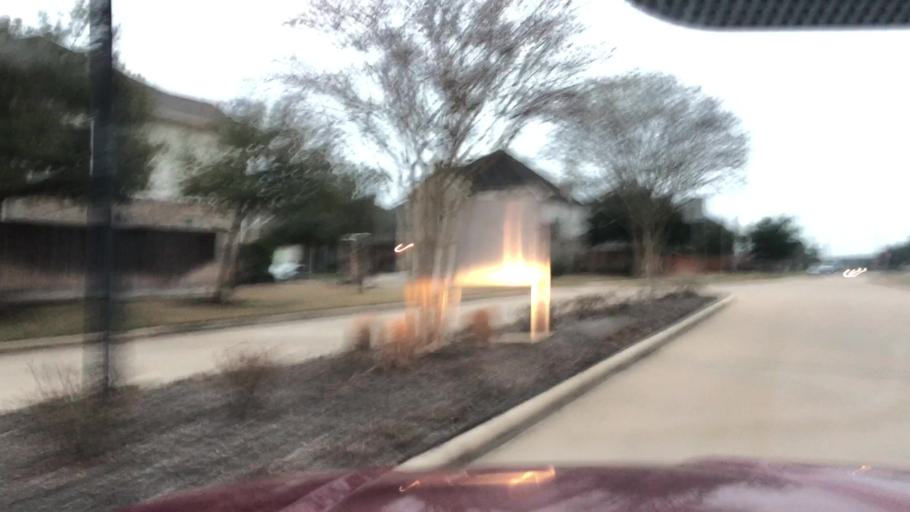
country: US
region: Texas
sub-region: Harris County
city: Tomball
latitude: 30.0861
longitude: -95.5557
